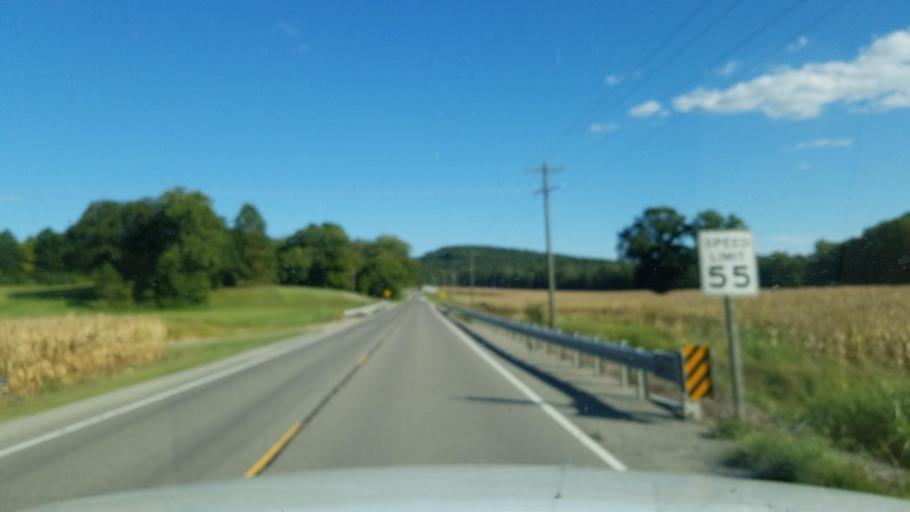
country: US
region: Illinois
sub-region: Hardin County
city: Rosiclare
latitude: 37.5791
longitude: -88.4346
